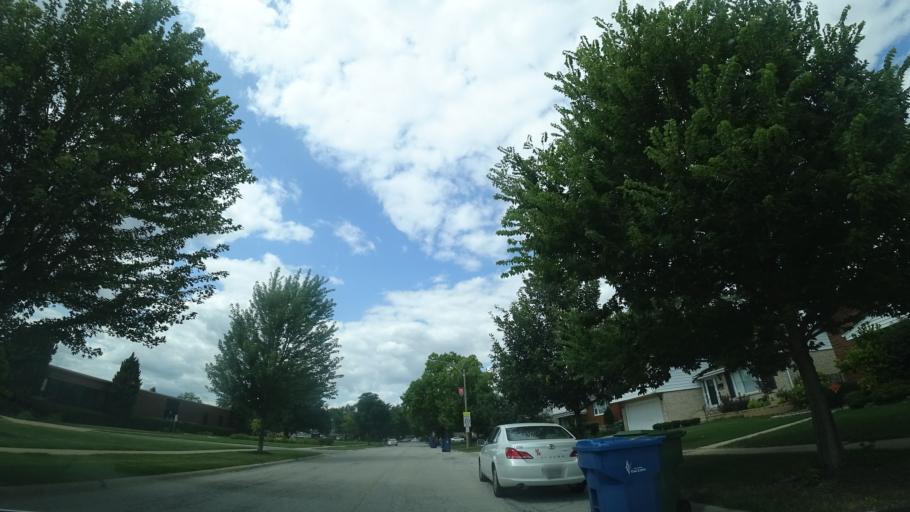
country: US
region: Illinois
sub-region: Cook County
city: Oak Lawn
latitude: 41.6969
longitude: -87.7351
